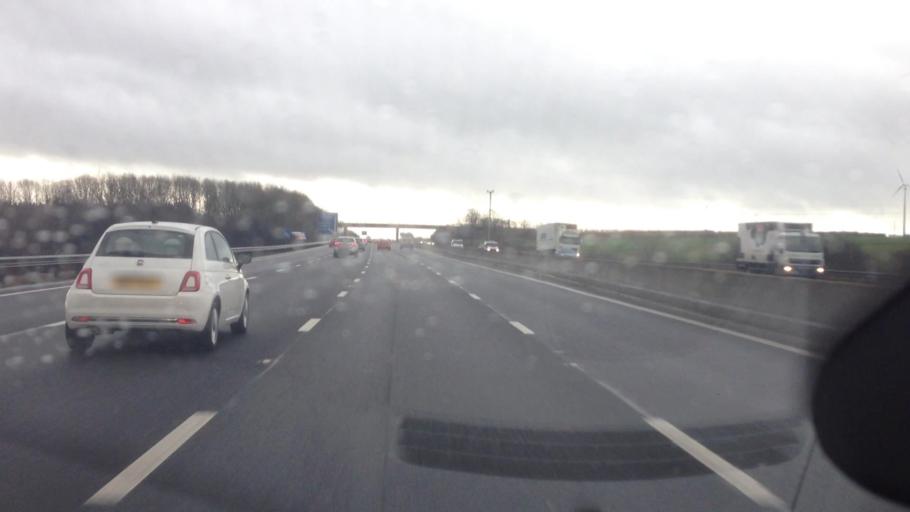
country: GB
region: England
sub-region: City and Borough of Wakefield
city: Ossett
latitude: 53.6931
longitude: -1.5575
